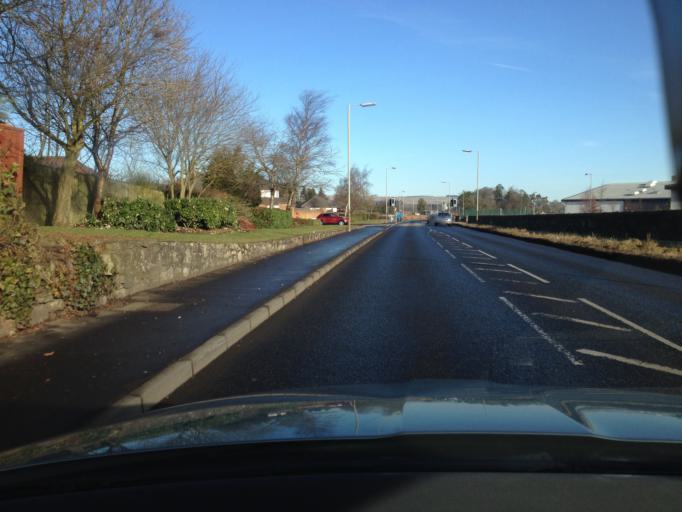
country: GB
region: Scotland
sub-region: Perth and Kinross
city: Kinross
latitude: 56.2160
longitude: -3.4268
